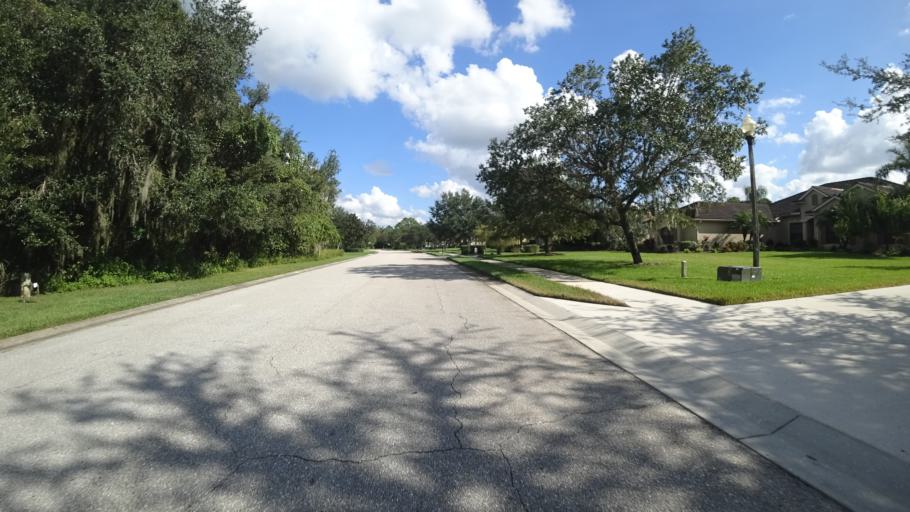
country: US
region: Florida
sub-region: Manatee County
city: Ellenton
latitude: 27.5460
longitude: -82.3831
